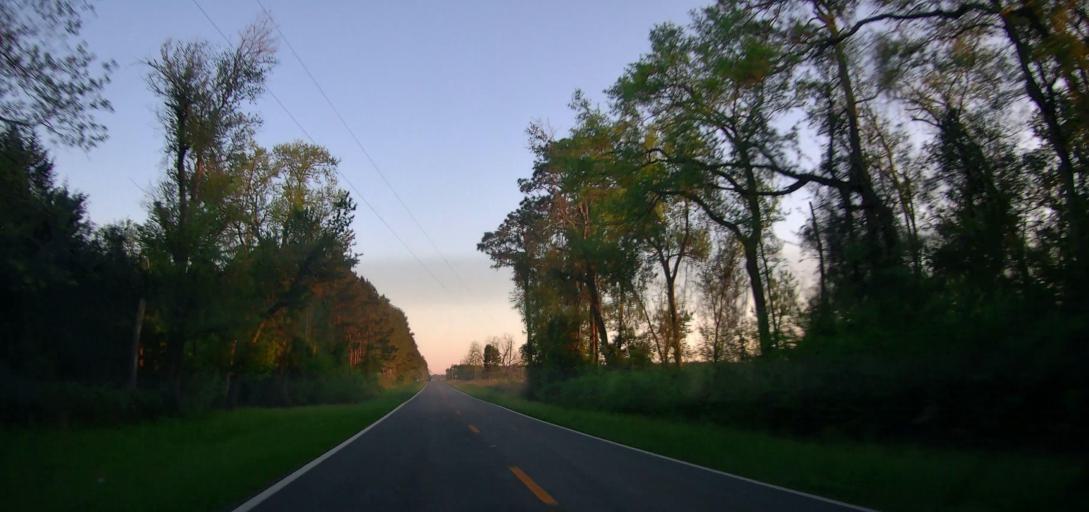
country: US
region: Georgia
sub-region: Ben Hill County
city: Fitzgerald
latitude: 31.7769
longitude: -83.3845
